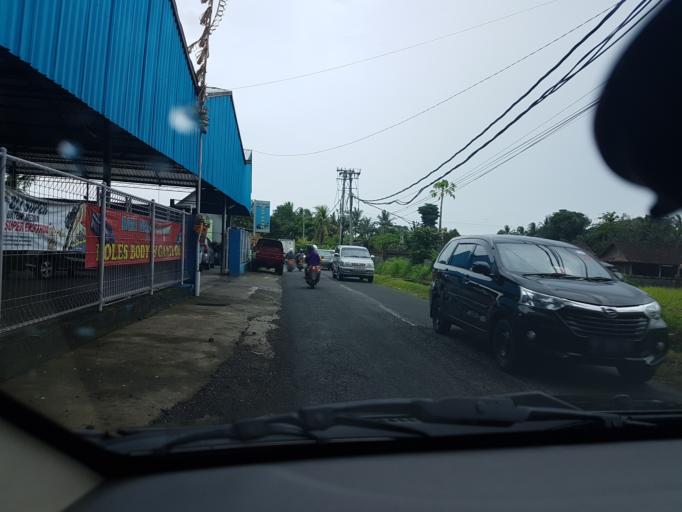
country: ID
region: Bali
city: Banjar Pande
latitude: -8.5210
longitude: 115.2393
